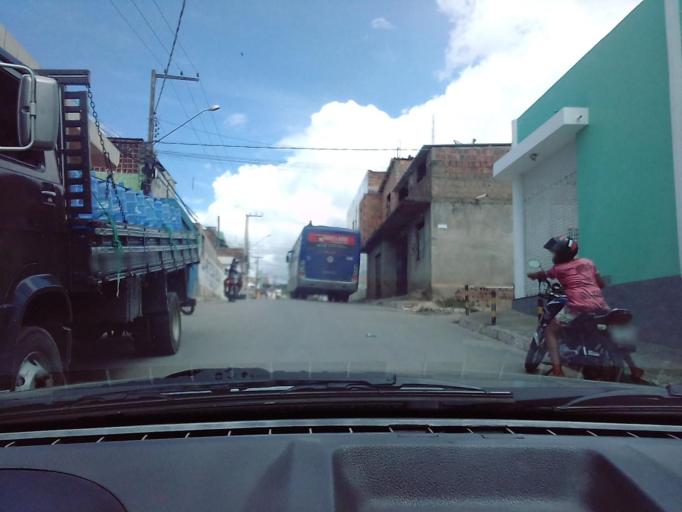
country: BR
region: Pernambuco
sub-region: Vitoria De Santo Antao
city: Vitoria de Santo Antao
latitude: -8.1290
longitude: -35.2904
